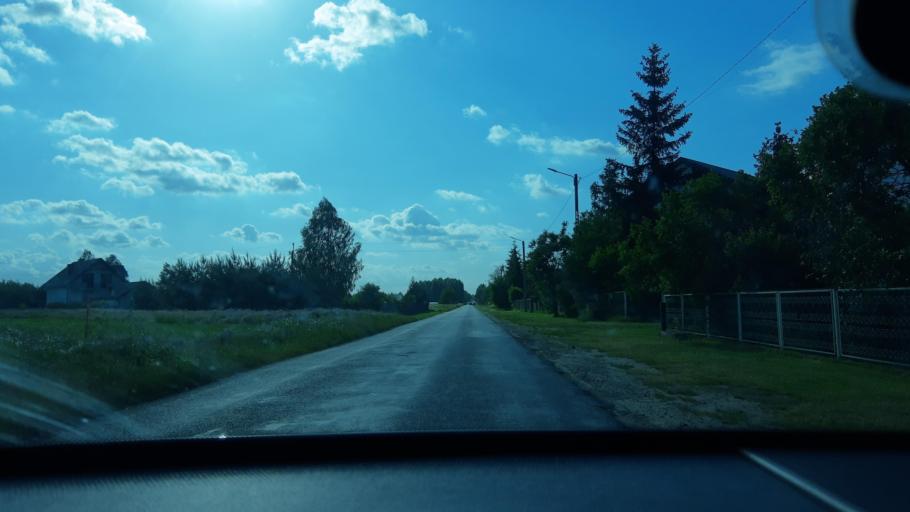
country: PL
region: Lodz Voivodeship
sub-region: Powiat zdunskowolski
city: Zapolice
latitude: 51.5397
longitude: 18.8032
